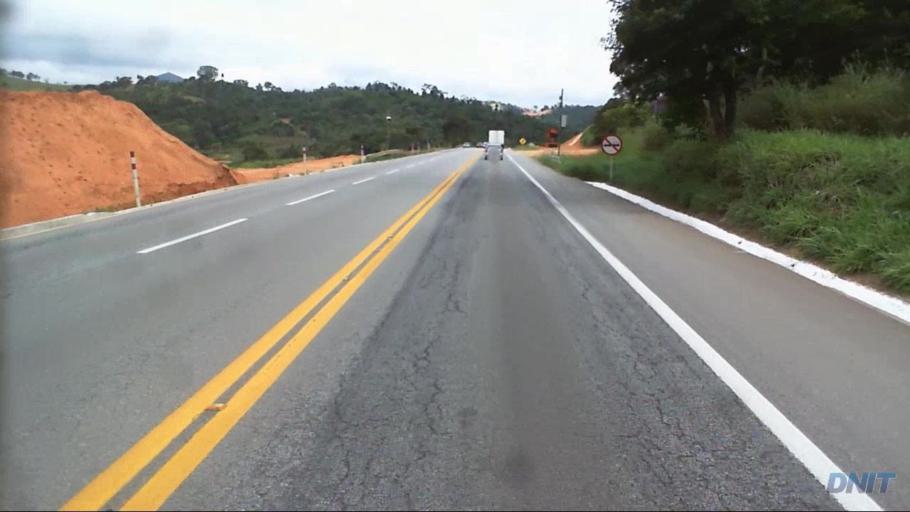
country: BR
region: Minas Gerais
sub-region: Caete
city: Caete
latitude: -19.7452
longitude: -43.6169
